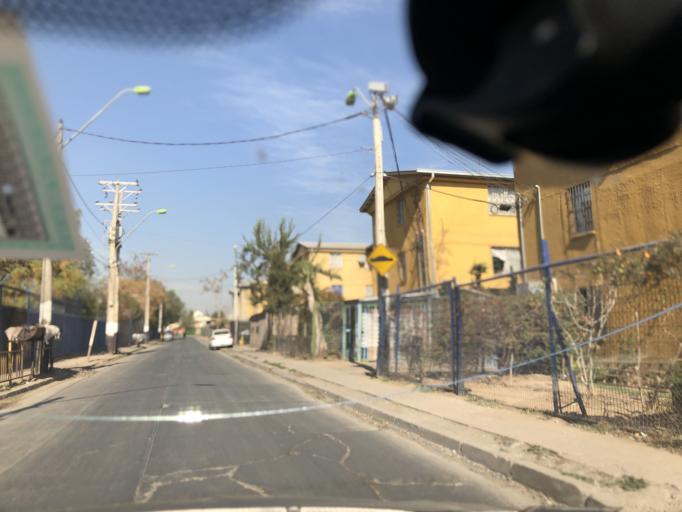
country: CL
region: Santiago Metropolitan
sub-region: Provincia de Santiago
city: La Pintana
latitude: -33.5921
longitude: -70.6027
